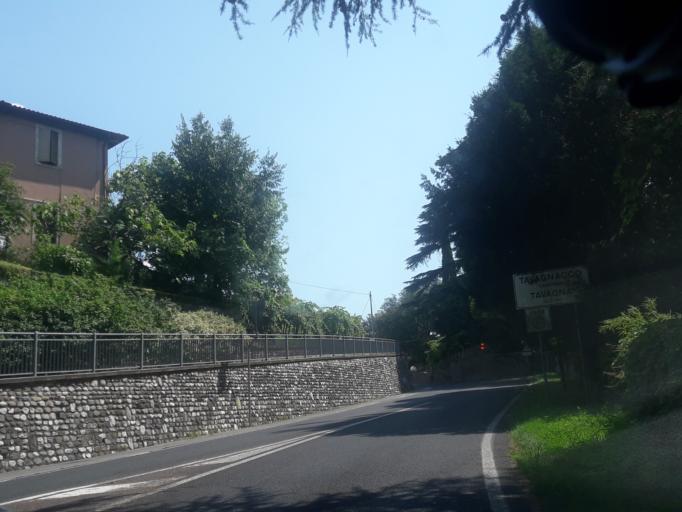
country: IT
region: Friuli Venezia Giulia
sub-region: Provincia di Udine
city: Reana del Roiale
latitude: 46.1287
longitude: 13.2104
